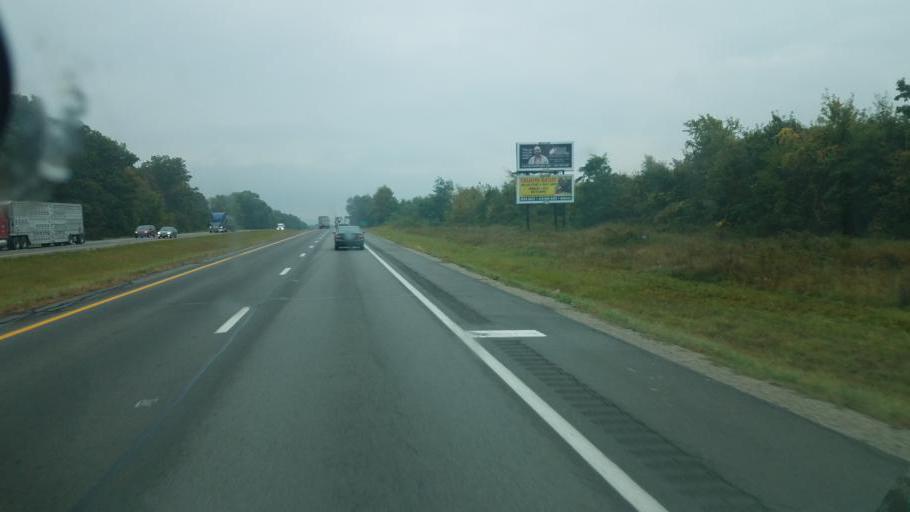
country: US
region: Ohio
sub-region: Richland County
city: Lincoln Heights
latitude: 40.7783
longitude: -82.4394
